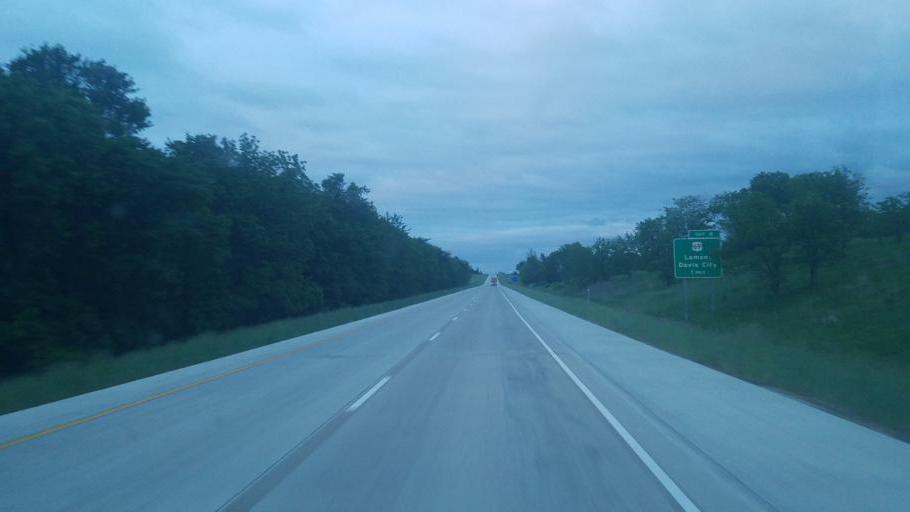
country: US
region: Iowa
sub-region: Decatur County
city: Lamoni
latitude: 40.6055
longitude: -93.9035
